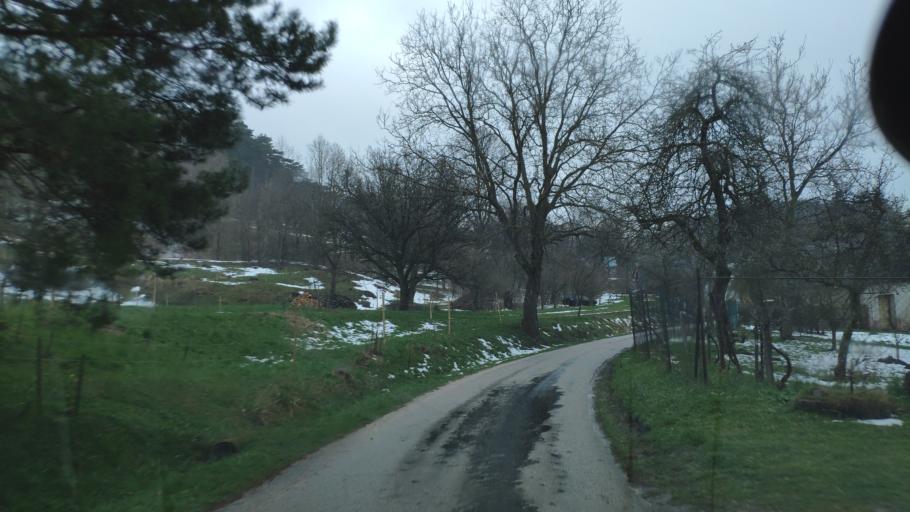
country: SK
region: Nitriansky
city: Stara Tura
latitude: 48.8286
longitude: 17.7052
